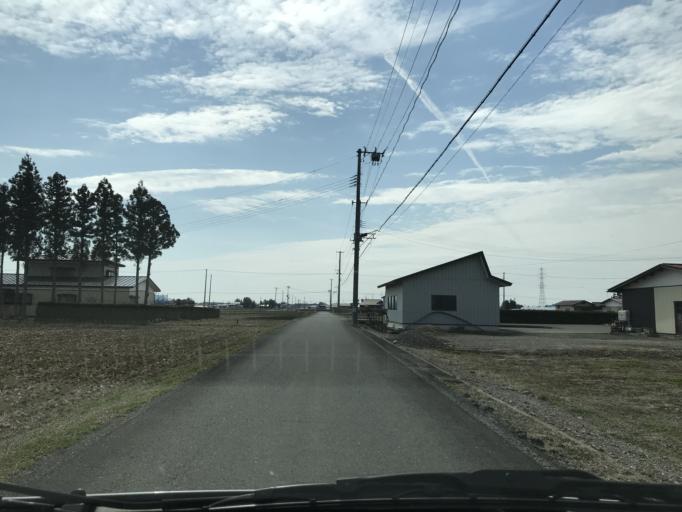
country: JP
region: Iwate
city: Mizusawa
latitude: 39.1553
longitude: 141.0845
